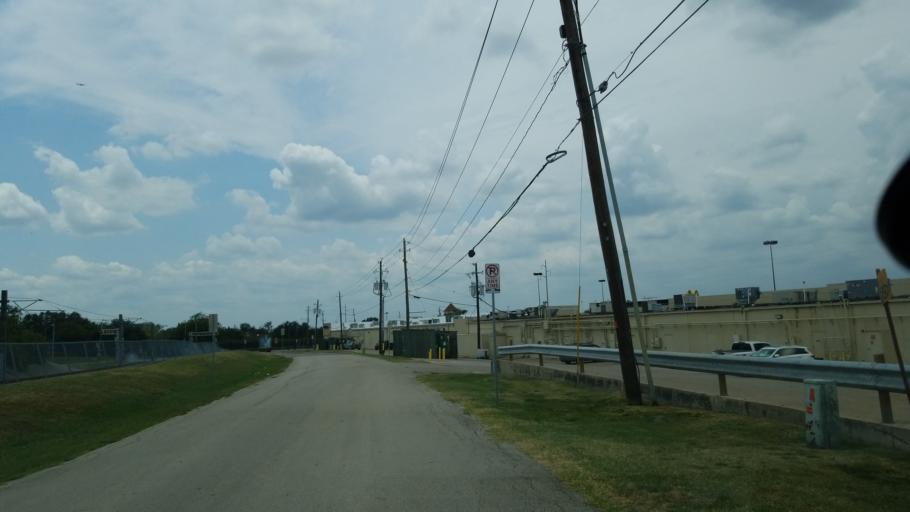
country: US
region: Texas
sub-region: Dallas County
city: Richardson
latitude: 32.8956
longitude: -96.7203
